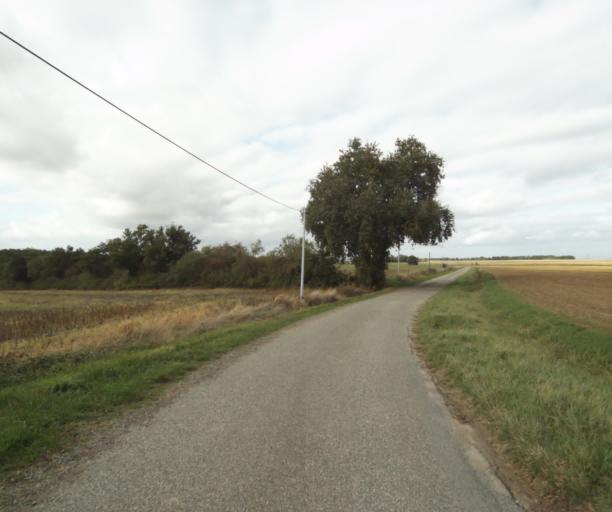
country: FR
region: Midi-Pyrenees
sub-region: Departement du Tarn-et-Garonne
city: Beaumont-de-Lomagne
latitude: 43.8803
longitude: 1.0848
